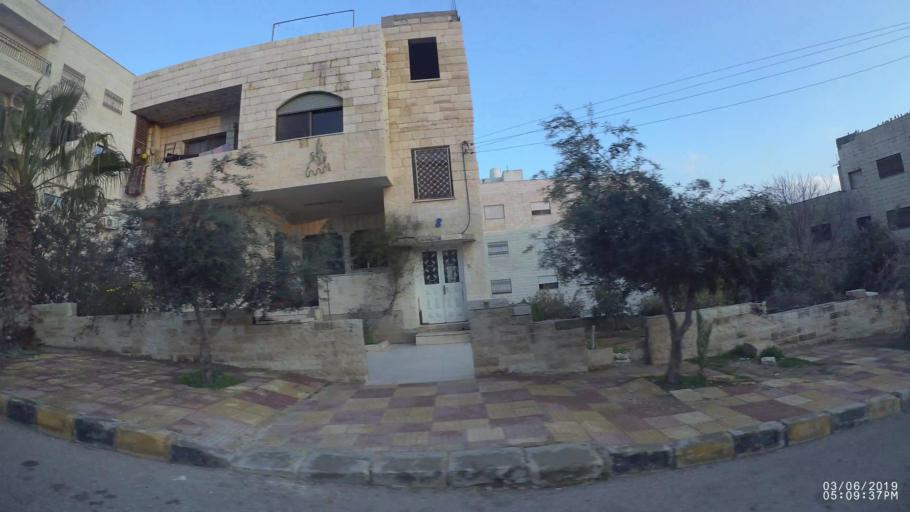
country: JO
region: Amman
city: Amman
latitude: 31.9926
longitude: 35.9509
